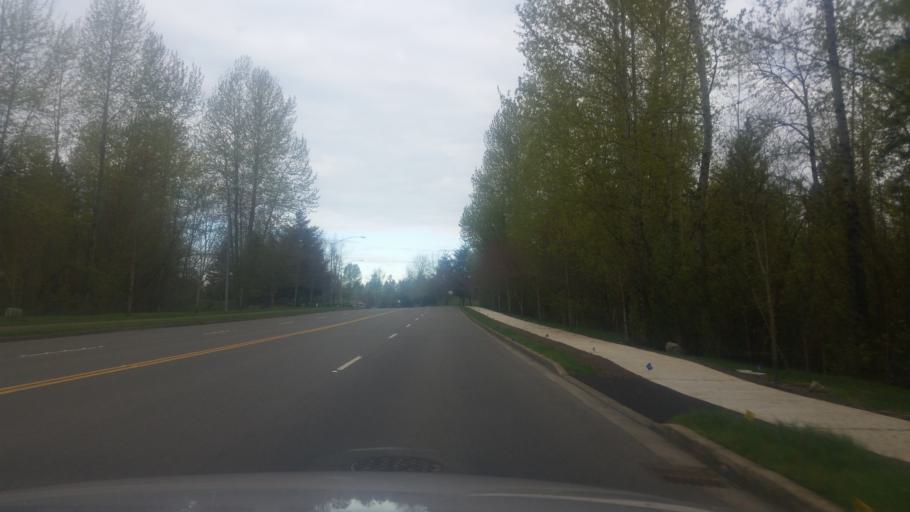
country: US
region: Washington
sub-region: Pierce County
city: South Hill
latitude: 47.1134
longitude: -122.2619
